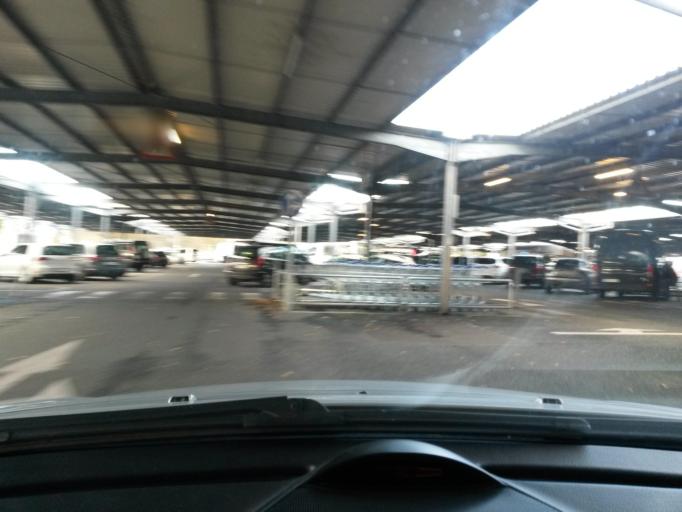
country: DE
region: Hamburg
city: Farmsen-Berne
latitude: 53.6189
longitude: 10.1552
